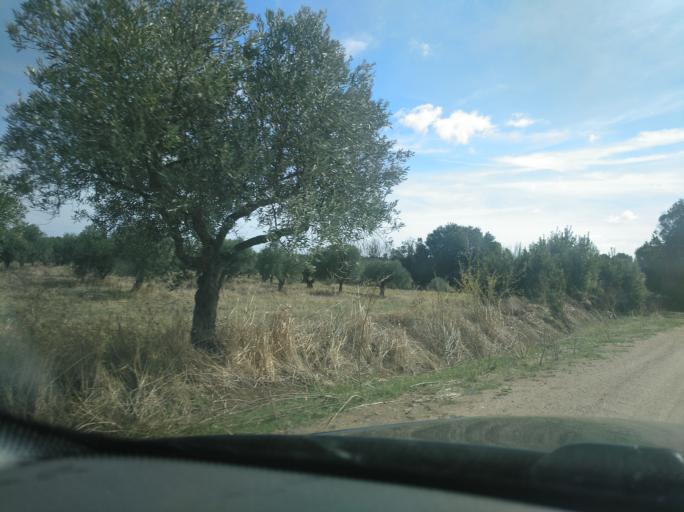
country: PT
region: Portalegre
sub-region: Campo Maior
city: Campo Maior
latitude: 39.0451
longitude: -7.0448
